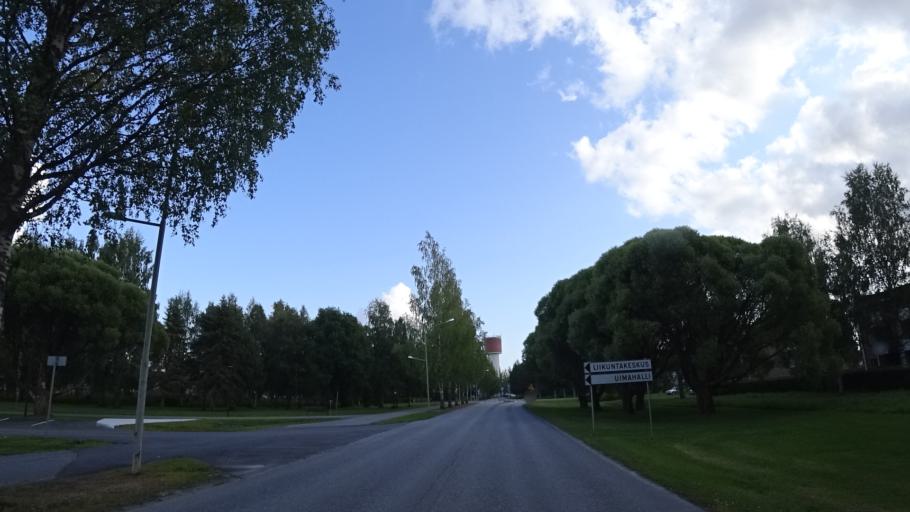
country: FI
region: North Karelia
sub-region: Pielisen Karjala
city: Lieksa
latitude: 63.3253
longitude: 30.0225
